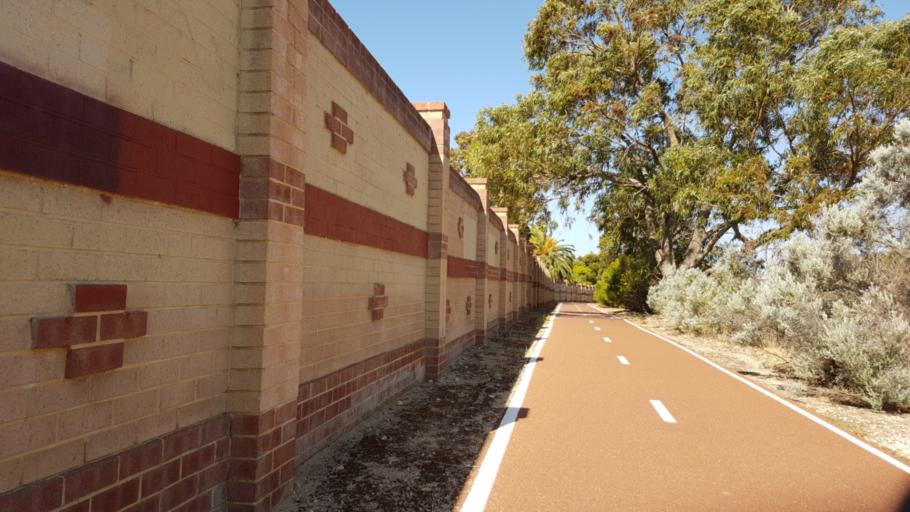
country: AU
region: Western Australia
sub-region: Stirling
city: Karrinyup
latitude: -31.8564
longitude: 115.7780
